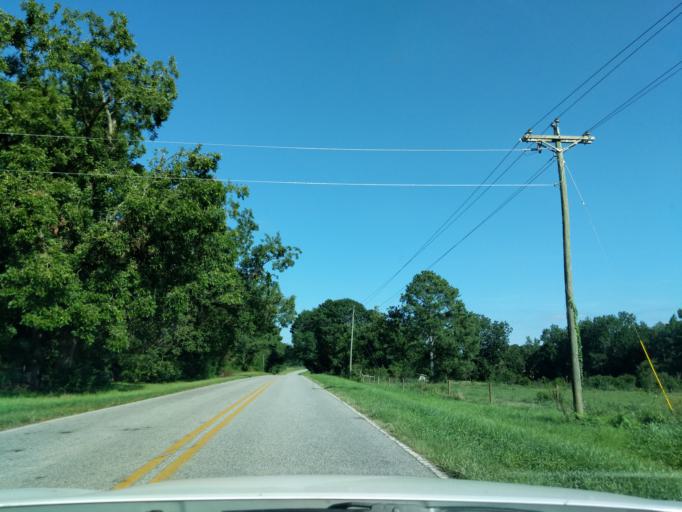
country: US
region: Georgia
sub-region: Oglethorpe County
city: Lexington
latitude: 33.9391
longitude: -83.0568
